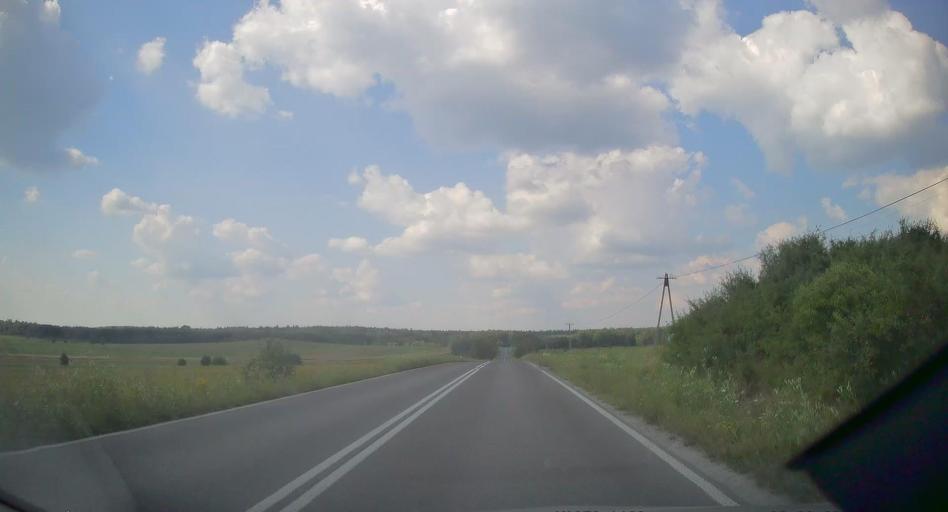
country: PL
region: Swietokrzyskie
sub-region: Powiat jedrzejowski
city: Malogoszcz
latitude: 50.8735
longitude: 20.2683
